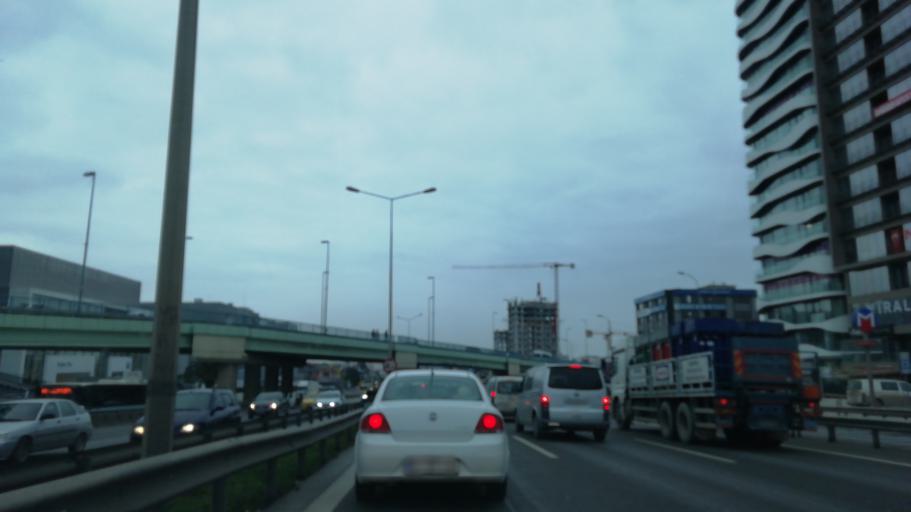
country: TR
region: Istanbul
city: Pendik
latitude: 40.8958
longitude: 29.2270
